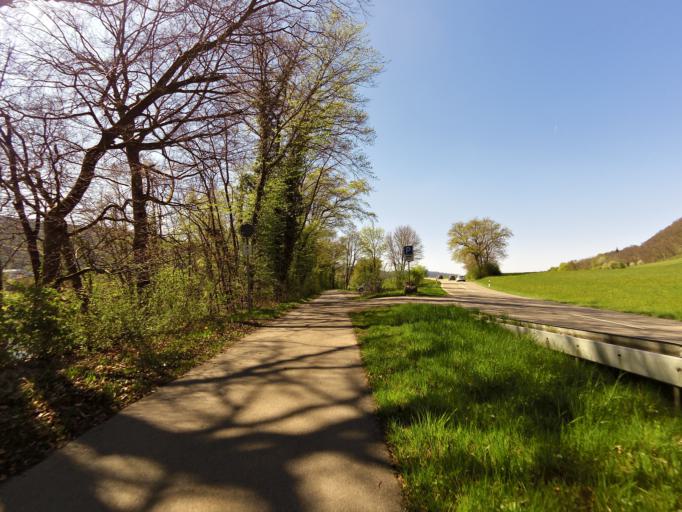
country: CH
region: Aargau
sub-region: Bezirk Zurzach
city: Bad Zurzach
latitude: 47.5715
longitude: 8.3491
